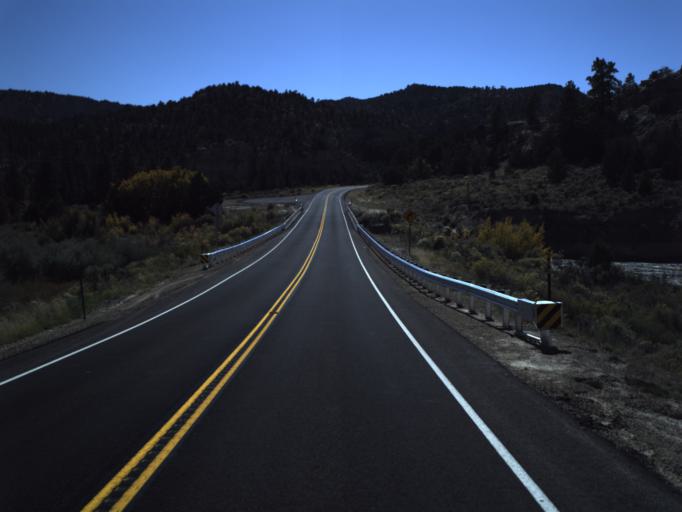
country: US
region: Utah
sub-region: Garfield County
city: Panguitch
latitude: 37.6146
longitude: -111.8957
